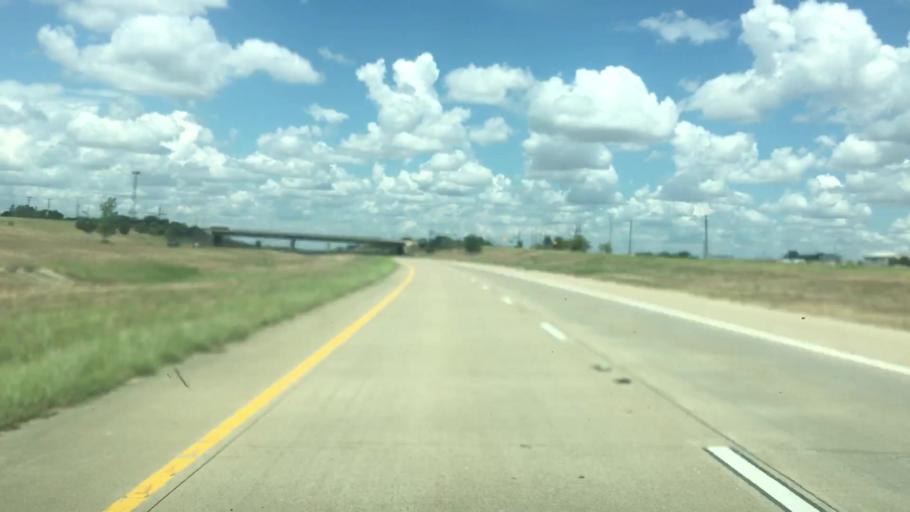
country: US
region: Texas
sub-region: Williamson County
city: Georgetown
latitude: 30.6384
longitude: -97.6286
